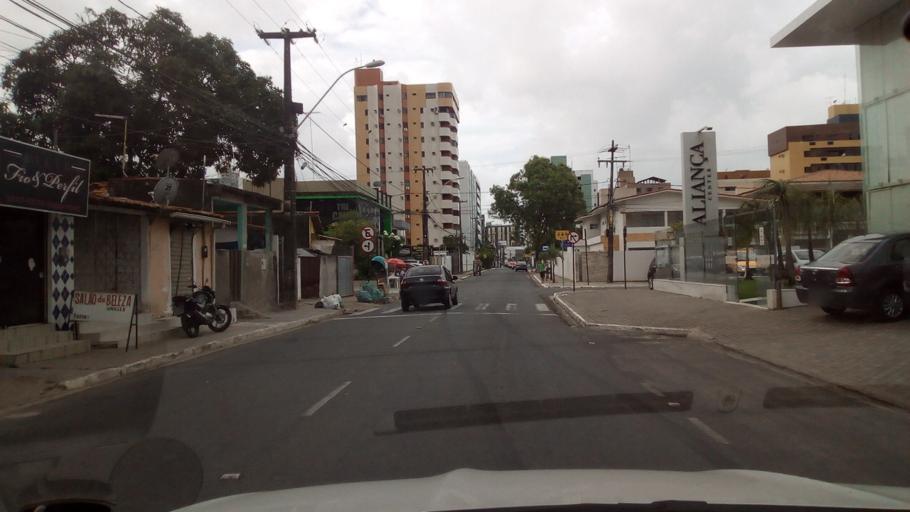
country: BR
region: Paraiba
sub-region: Joao Pessoa
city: Joao Pessoa
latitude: -7.1283
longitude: -34.8256
